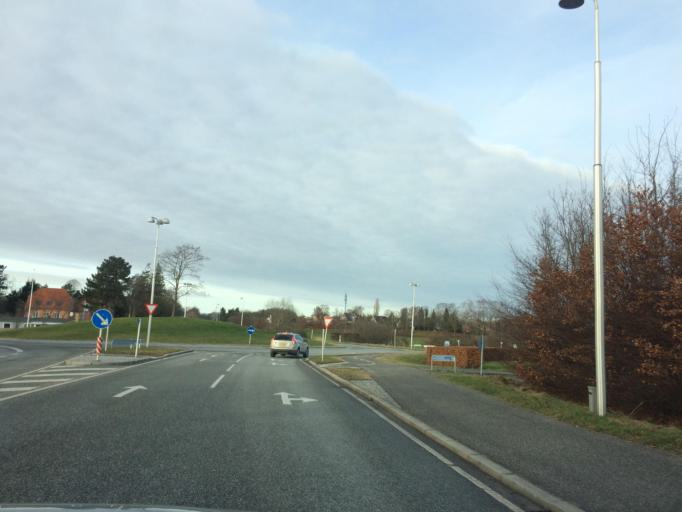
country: DK
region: Capital Region
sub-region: Fredensborg Kommune
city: Fredensborg
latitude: 55.9645
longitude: 12.4070
